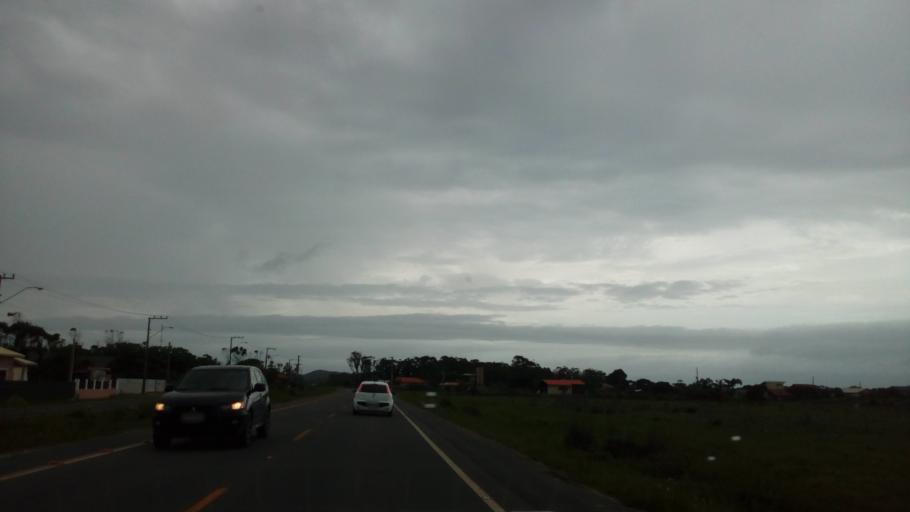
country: BR
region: Santa Catarina
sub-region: Laguna
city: Laguna
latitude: -28.5520
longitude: -48.7989
